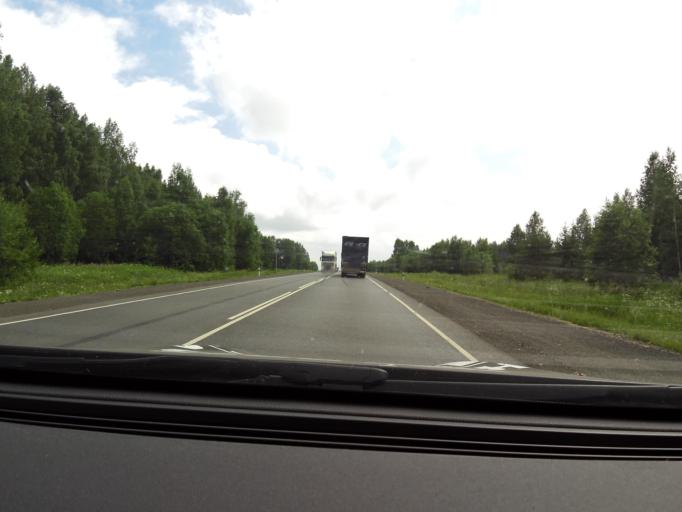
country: RU
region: Perm
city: Ust'-Kishert'
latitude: 57.1763
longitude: 57.1367
